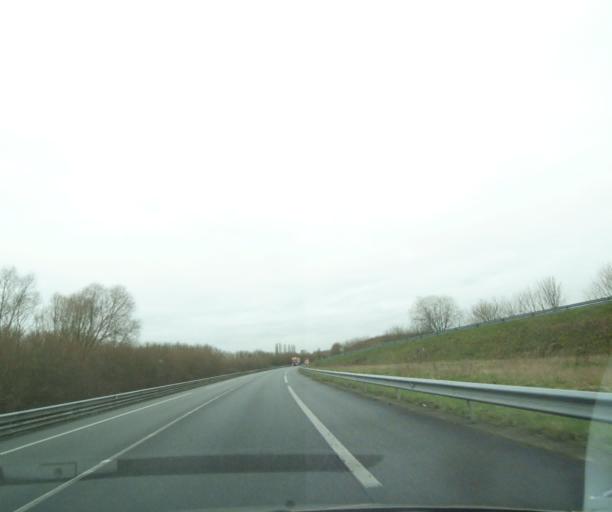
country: FR
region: Picardie
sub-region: Departement de l'Oise
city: Noyon
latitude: 49.5738
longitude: 3.0346
